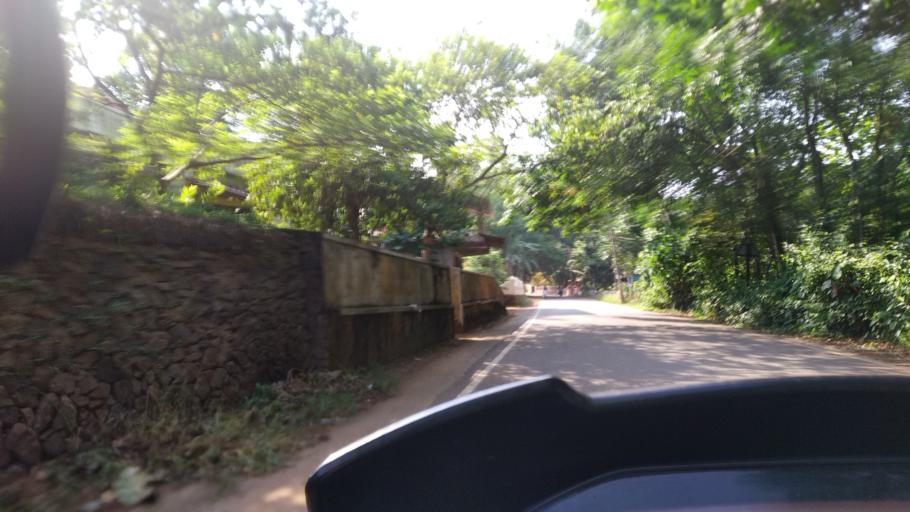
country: IN
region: Kerala
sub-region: Ernakulam
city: Piravam
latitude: 9.8617
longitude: 76.5168
